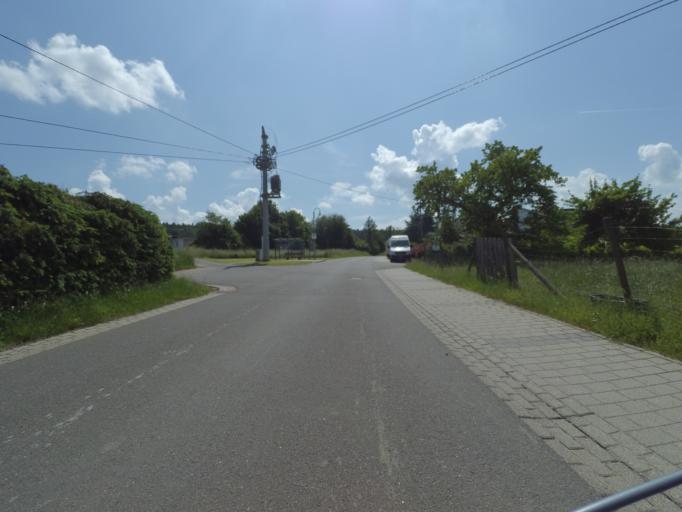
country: DE
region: Rheinland-Pfalz
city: Mermuth
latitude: 50.1693
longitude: 7.4836
